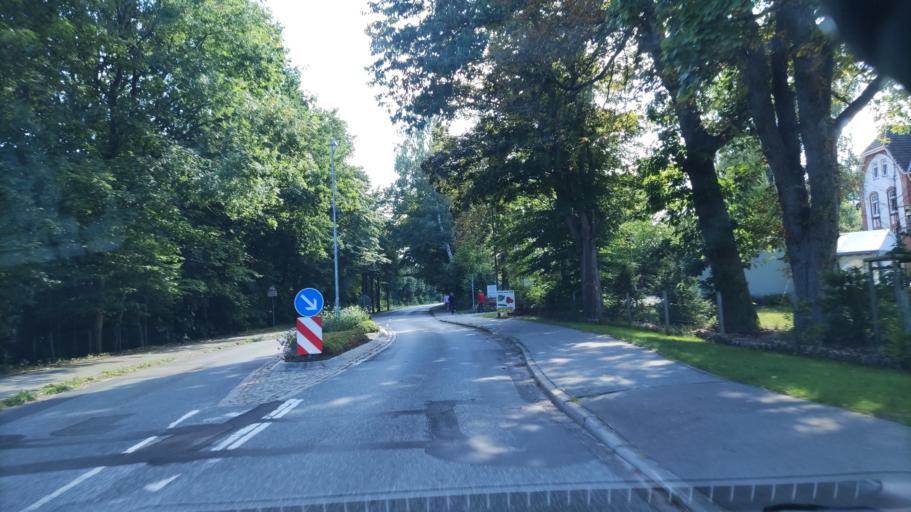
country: DE
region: Schleswig-Holstein
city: Aukrug
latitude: 54.0803
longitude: 9.7792
